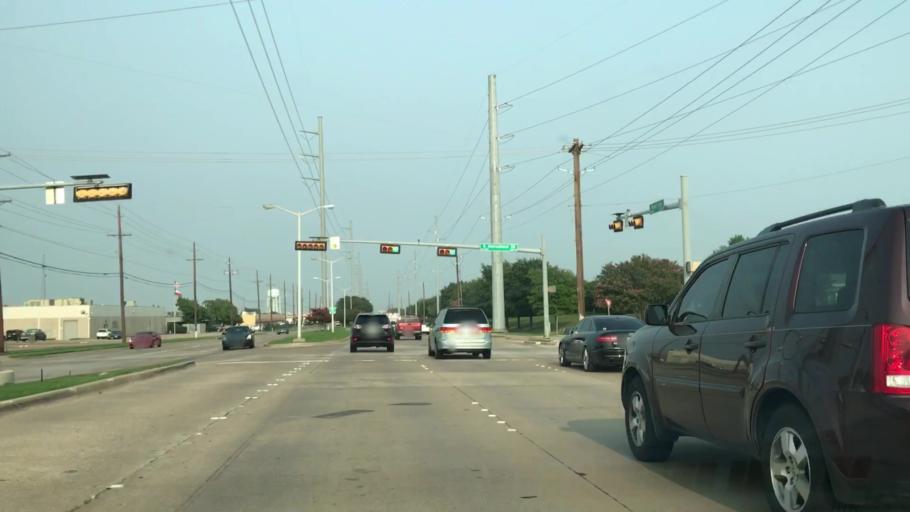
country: US
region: Texas
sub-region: Dallas County
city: Garland
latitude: 32.9091
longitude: -96.6731
